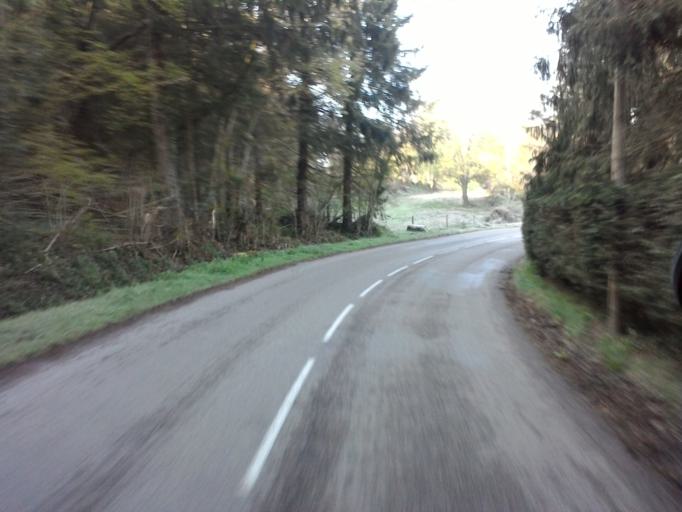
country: FR
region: Bourgogne
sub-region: Departement de la Cote-d'Or
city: Saulieu
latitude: 47.2467
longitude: 4.0729
